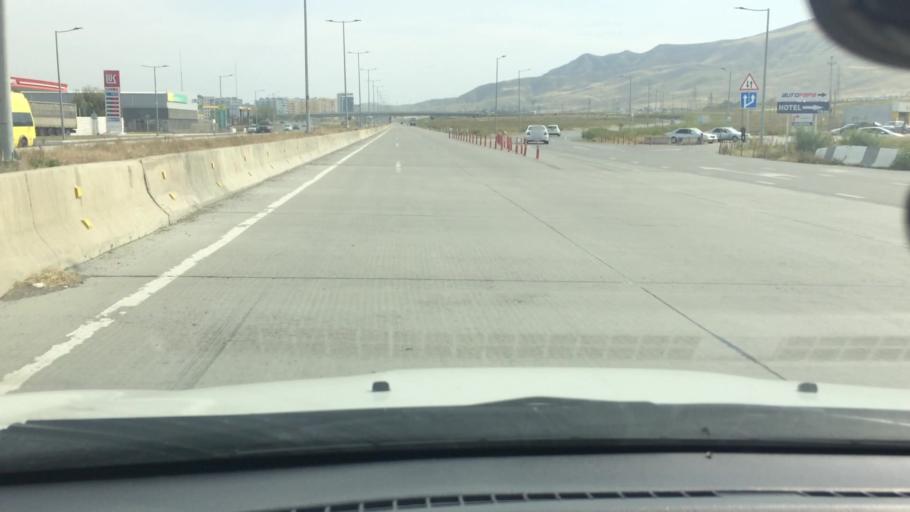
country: GE
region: Kvemo Kartli
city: Rust'avi
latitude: 41.5755
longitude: 44.9568
